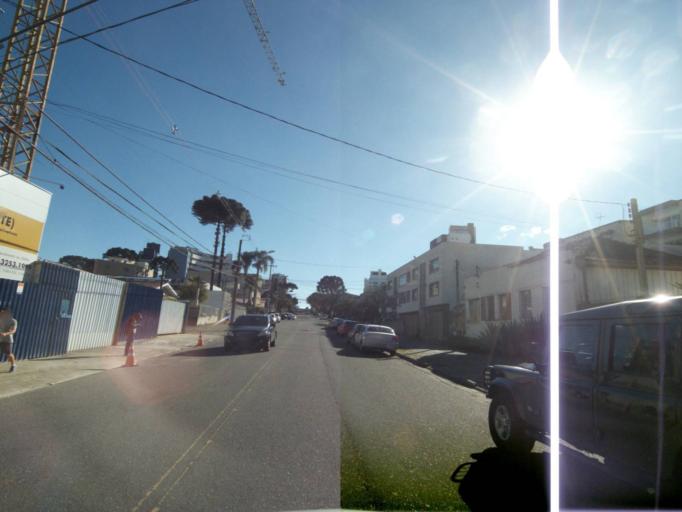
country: BR
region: Parana
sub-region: Curitiba
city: Curitiba
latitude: -25.4099
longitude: -49.2618
